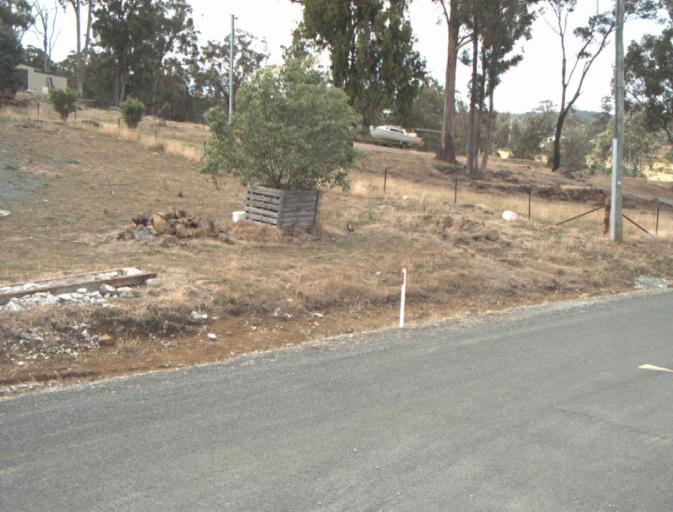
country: AU
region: Tasmania
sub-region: Launceston
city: Mayfield
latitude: -41.3035
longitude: 147.0404
